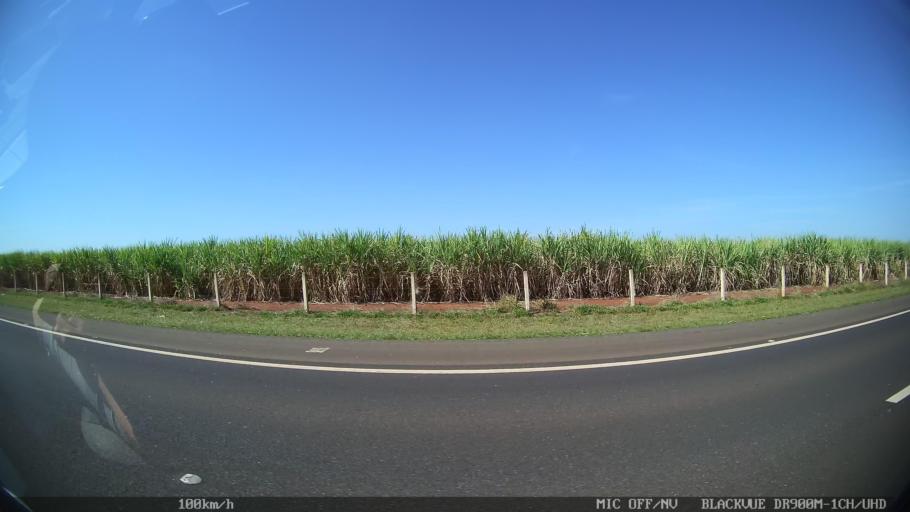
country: BR
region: Sao Paulo
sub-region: Batatais
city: Batatais
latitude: -20.7773
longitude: -47.5469
